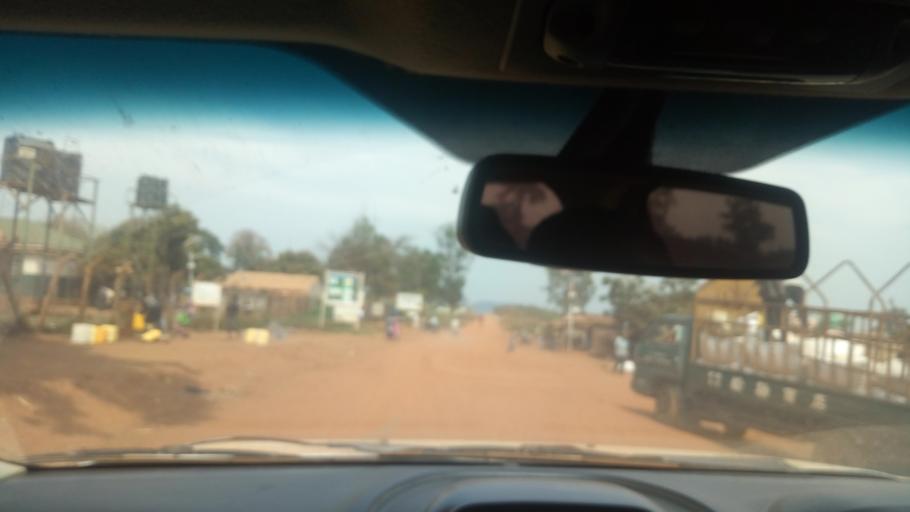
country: UG
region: Western Region
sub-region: Kiryandongo District
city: Kiryandongo
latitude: 1.9394
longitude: 32.1693
